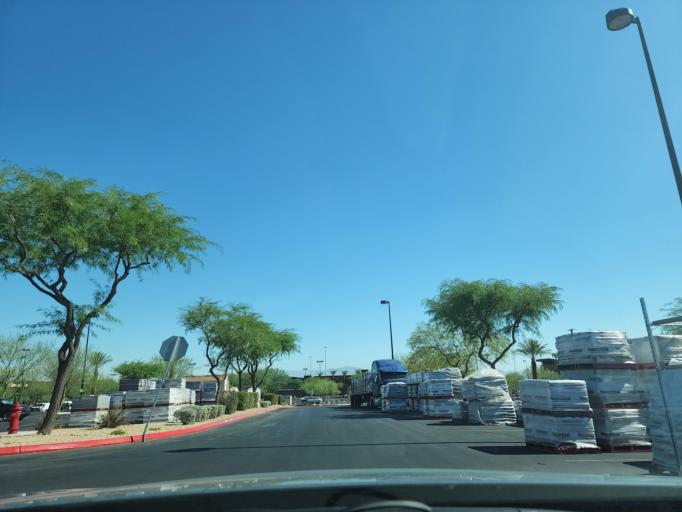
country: US
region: Nevada
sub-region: Clark County
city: Enterprise
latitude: 36.0624
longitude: -115.2437
